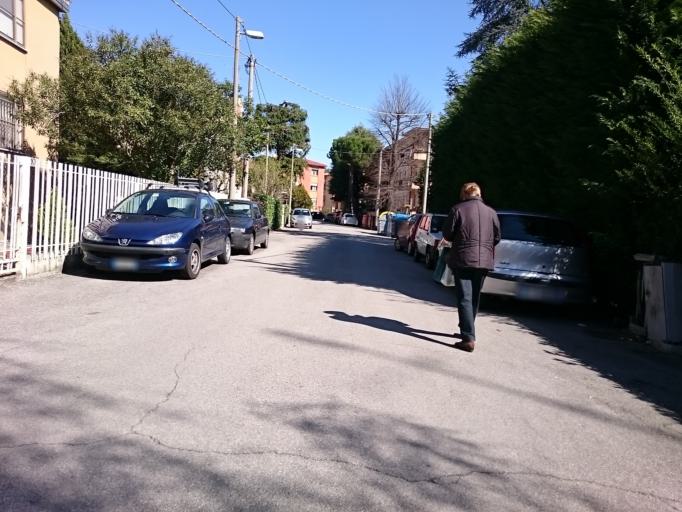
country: IT
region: Veneto
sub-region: Provincia di Padova
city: Padova
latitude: 45.4001
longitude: 11.8974
